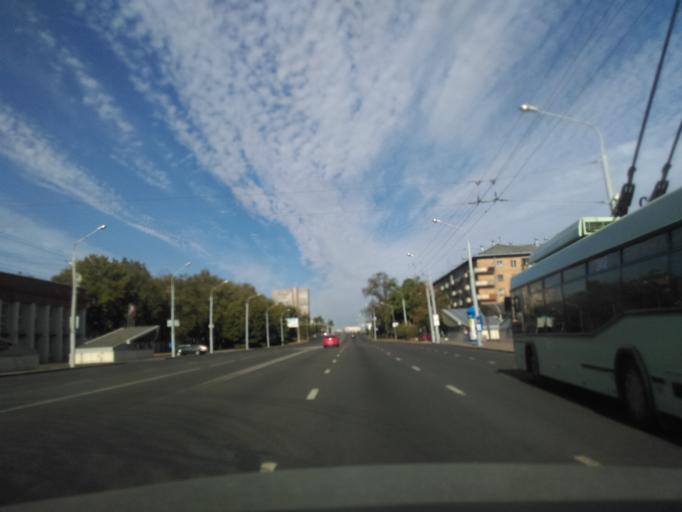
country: BY
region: Minsk
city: Minsk
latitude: 53.8832
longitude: 27.5931
